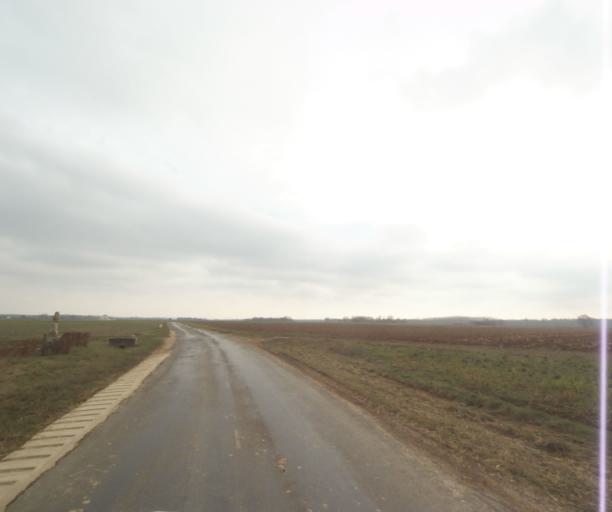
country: FR
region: Champagne-Ardenne
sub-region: Departement de la Haute-Marne
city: Villiers-en-Lieu
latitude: 48.6785
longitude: 4.8516
